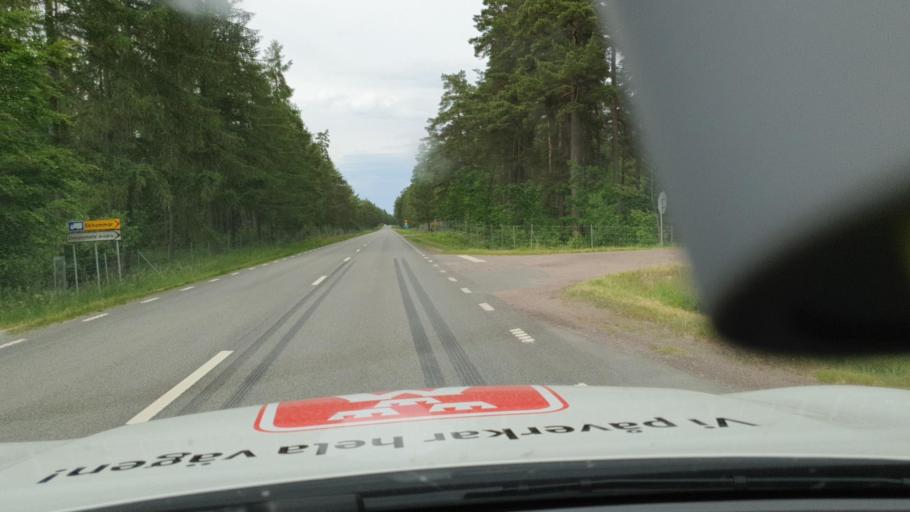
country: SE
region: Vaestra Goetaland
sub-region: Hjo Kommun
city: Hjo
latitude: 58.3657
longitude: 14.3522
